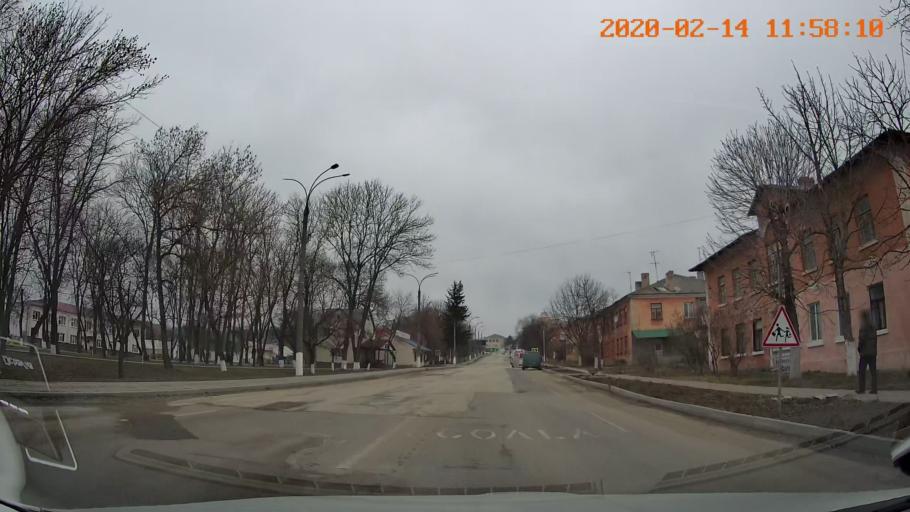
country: RO
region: Botosani
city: Radauti
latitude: 48.2646
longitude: 26.8036
